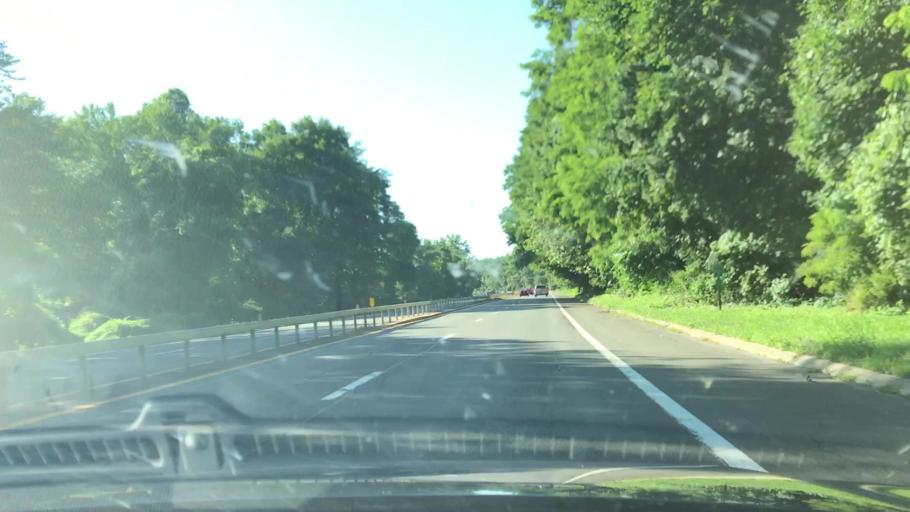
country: US
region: New York
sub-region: Westchester County
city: Valhalla
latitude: 41.0798
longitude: -73.7807
